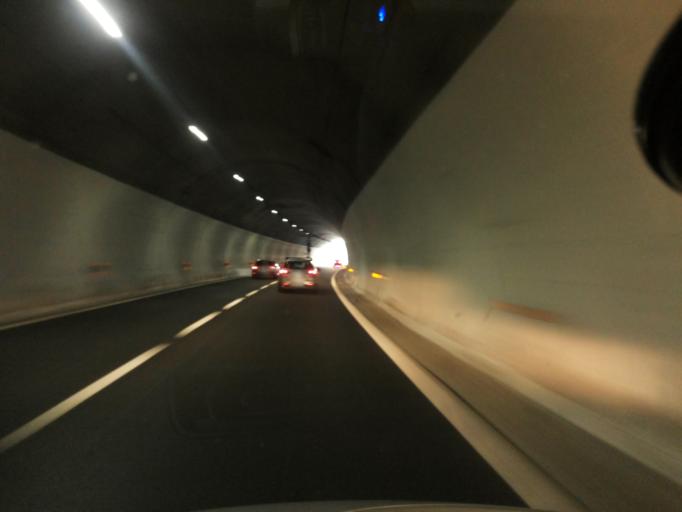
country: IT
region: Piedmont
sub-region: Provincia di Novara
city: Nebbiuno
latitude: 45.8094
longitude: 8.5340
